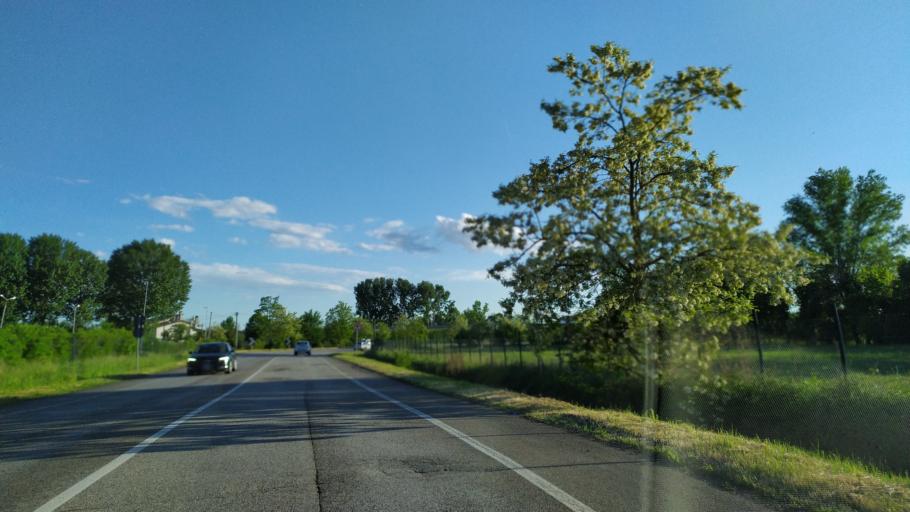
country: IT
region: Veneto
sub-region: Provincia di Padova
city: Taggi
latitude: 45.4524
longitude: 11.8342
